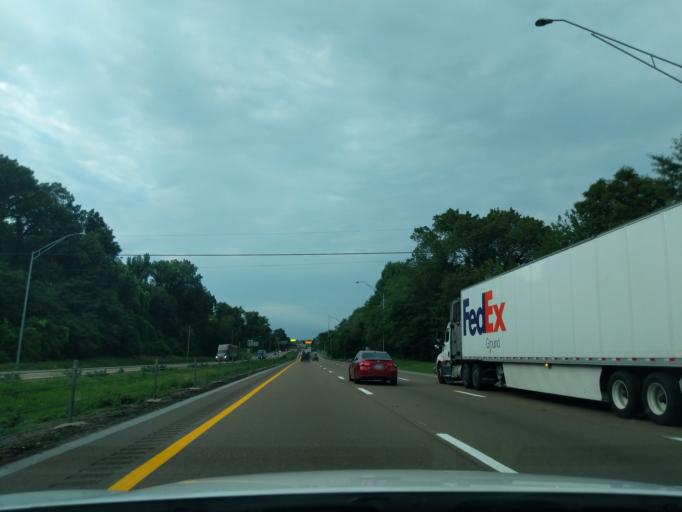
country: US
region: Tennessee
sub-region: Shelby County
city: New South Memphis
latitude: 35.0943
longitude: -90.0765
